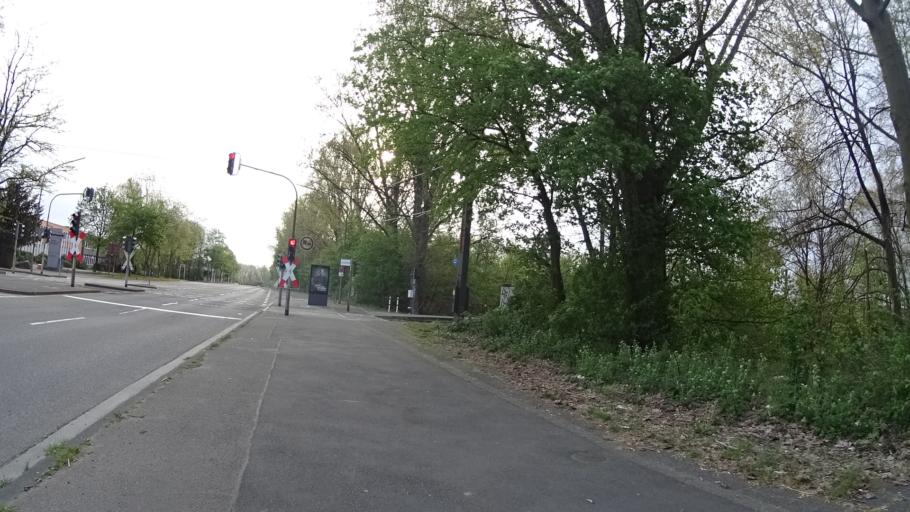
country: DE
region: North Rhine-Westphalia
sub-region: Regierungsbezirk Koln
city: Nippes
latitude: 50.9958
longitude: 6.9549
